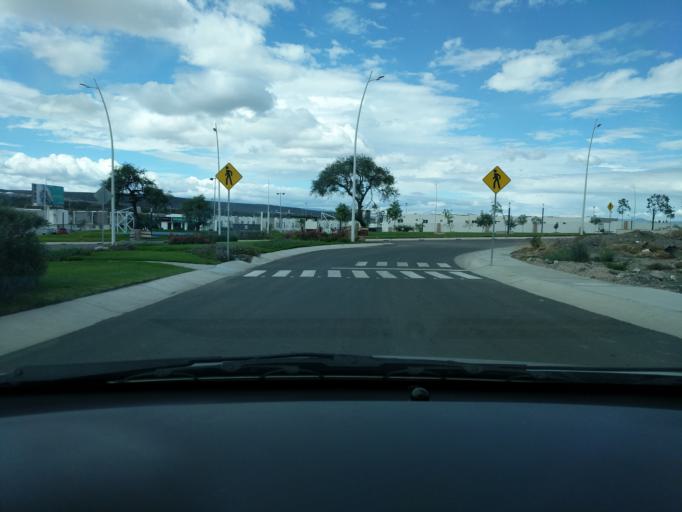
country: MX
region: Queretaro
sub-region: El Marques
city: El Pozo
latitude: 20.6462
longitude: -100.3114
